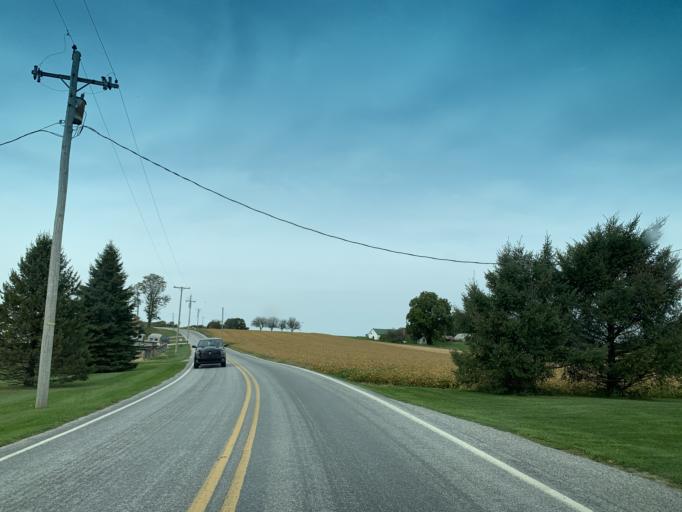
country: US
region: Pennsylvania
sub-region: York County
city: Windsor
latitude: 39.8660
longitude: -76.5114
